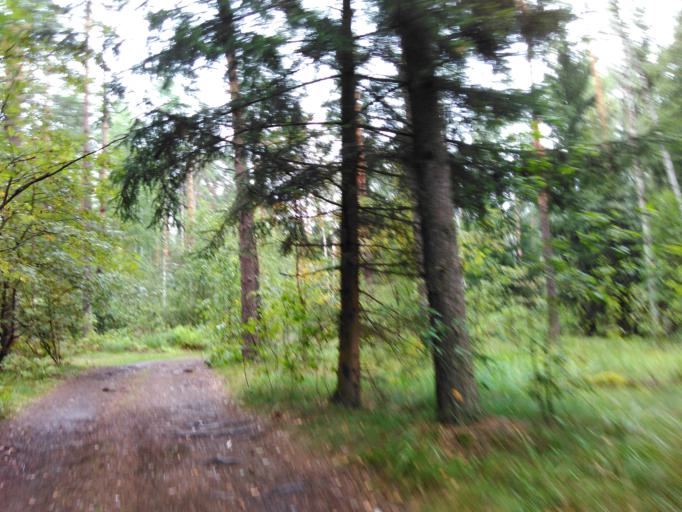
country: RU
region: Moskovskaya
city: Elektrogorsk
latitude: 55.9453
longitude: 38.6563
